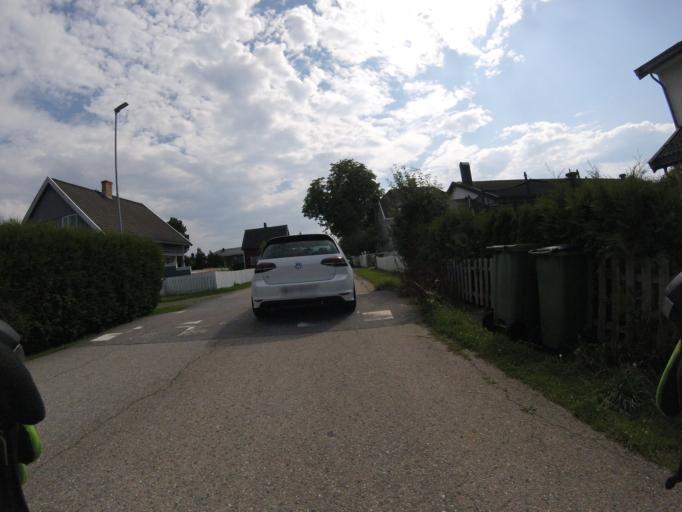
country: NO
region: Akershus
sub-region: Skedsmo
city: Lillestrom
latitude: 59.9559
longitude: 11.0665
